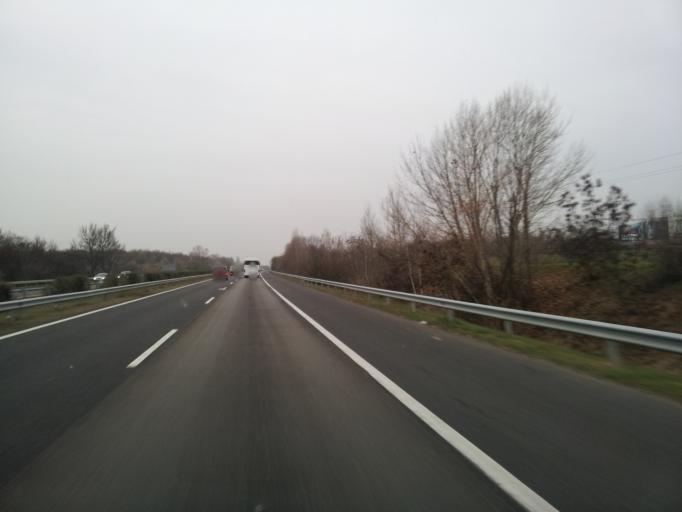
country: HU
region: Fejer
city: Pakozd
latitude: 47.2152
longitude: 18.5546
